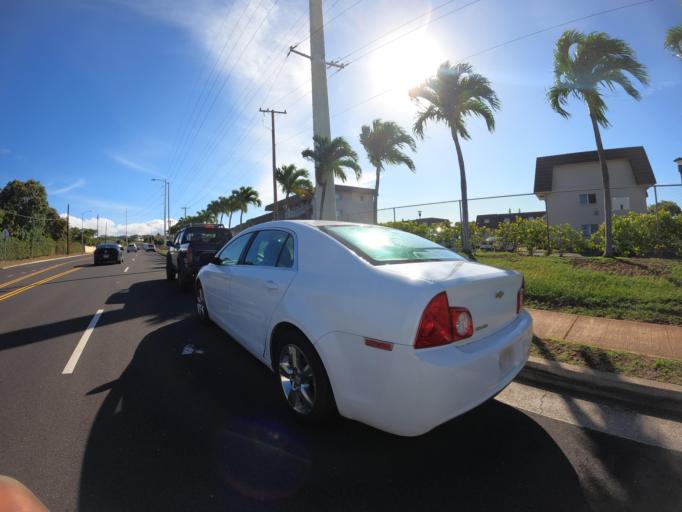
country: US
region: Hawaii
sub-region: Honolulu County
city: Halawa
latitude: 21.3584
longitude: -157.9261
